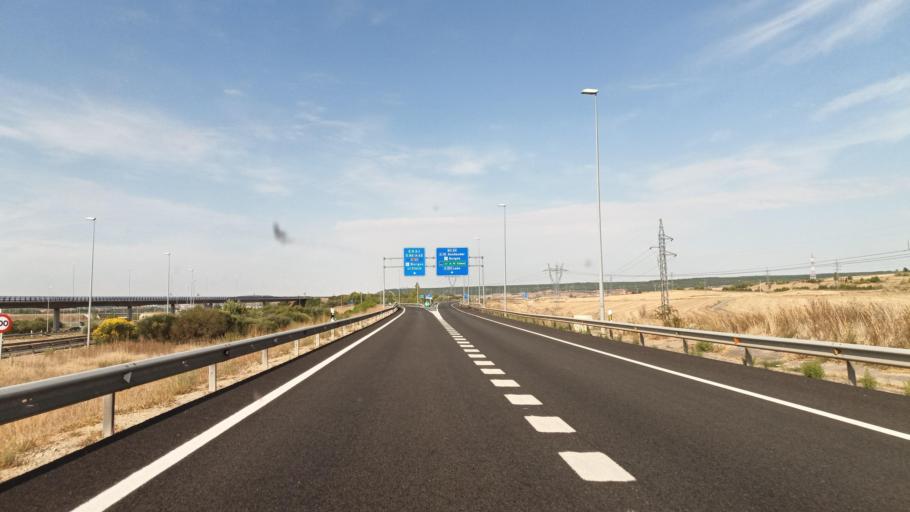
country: ES
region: Castille and Leon
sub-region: Provincia de Burgos
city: Hurones
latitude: 42.3713
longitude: -3.6315
